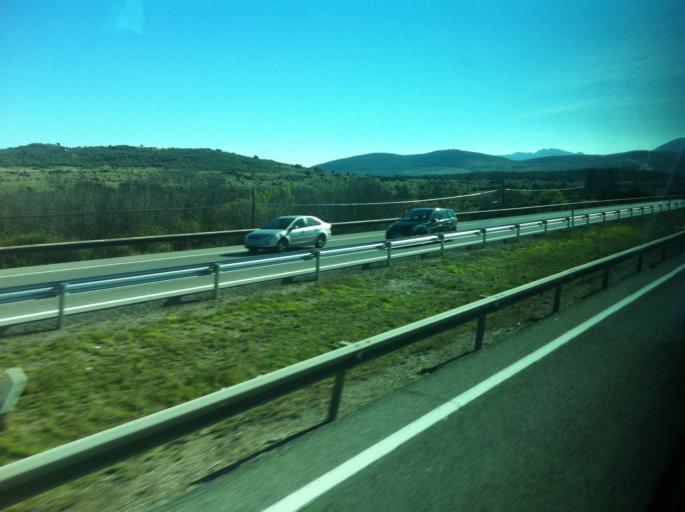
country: ES
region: Madrid
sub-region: Provincia de Madrid
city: Gascones
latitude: 41.0196
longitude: -3.6270
